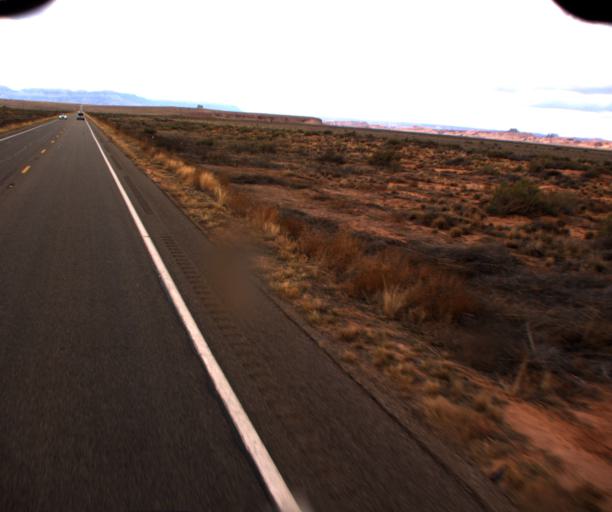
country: US
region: Arizona
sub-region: Navajo County
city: Kayenta
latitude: 36.7619
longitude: -110.0416
